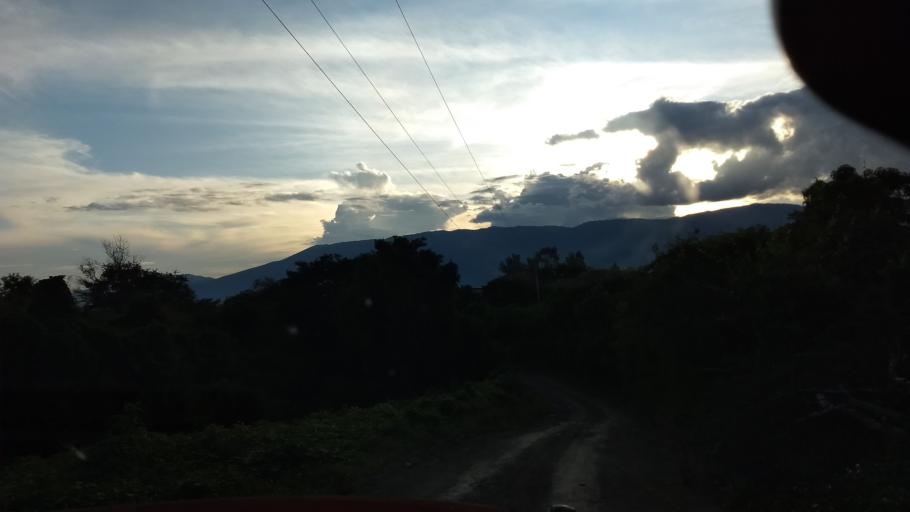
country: MX
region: Jalisco
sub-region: San Gabriel
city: Alista
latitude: 19.5007
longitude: -103.7661
